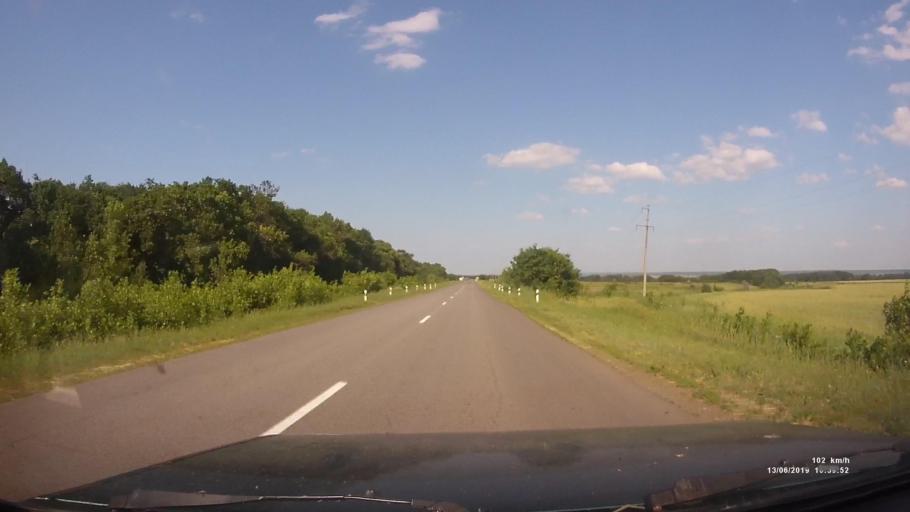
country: RU
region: Rostov
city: Kazanskaya
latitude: 49.9293
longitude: 41.3498
